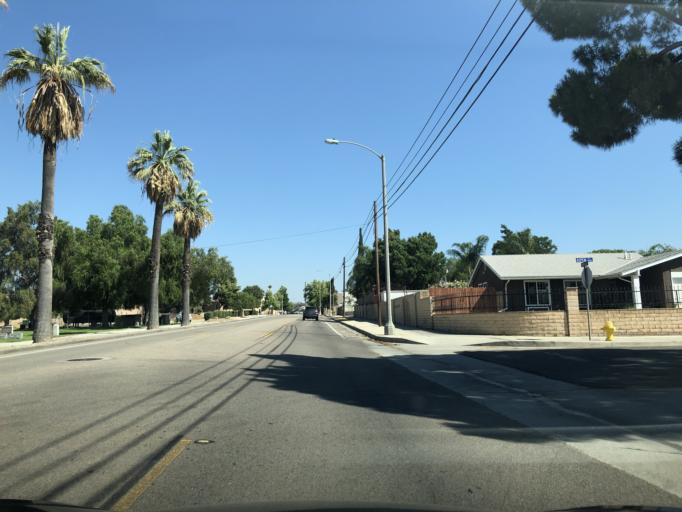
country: US
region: California
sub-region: Riverside County
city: Corona
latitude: 33.8673
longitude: -117.5474
